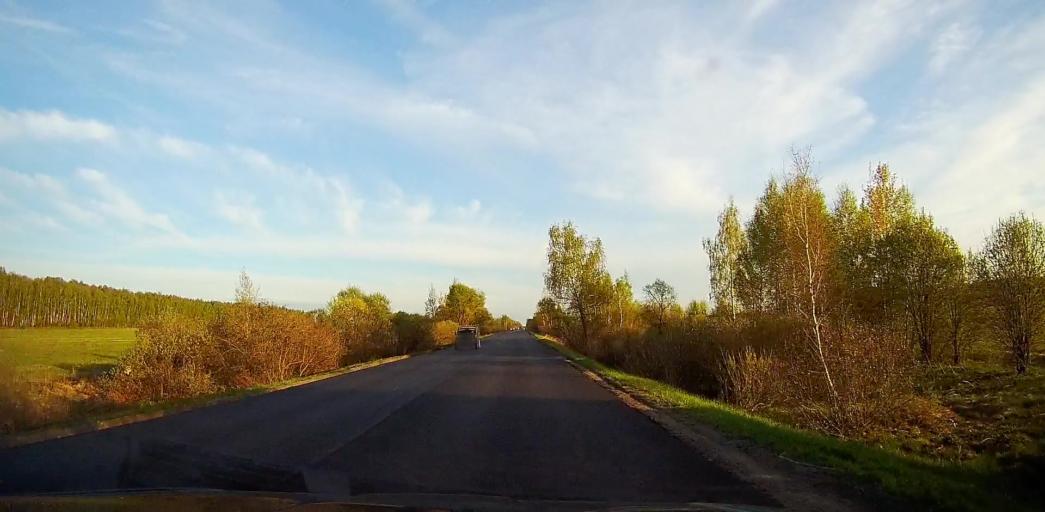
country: RU
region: Moskovskaya
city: Bronnitsy
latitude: 55.2847
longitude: 38.2163
